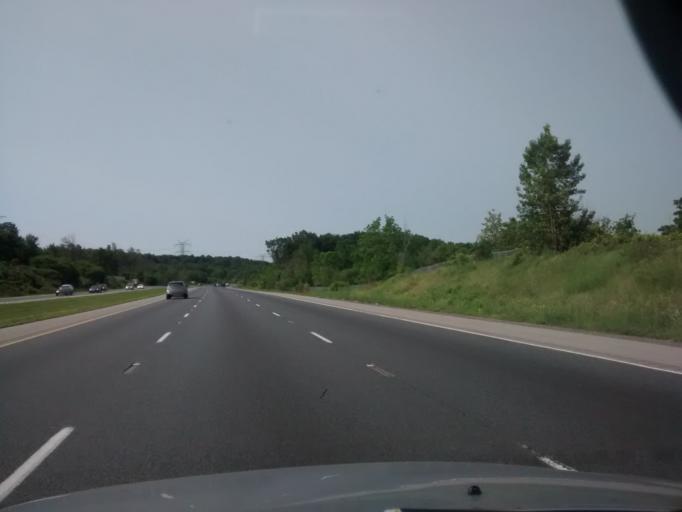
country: CA
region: Ontario
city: Hamilton
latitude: 43.2136
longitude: -79.8030
